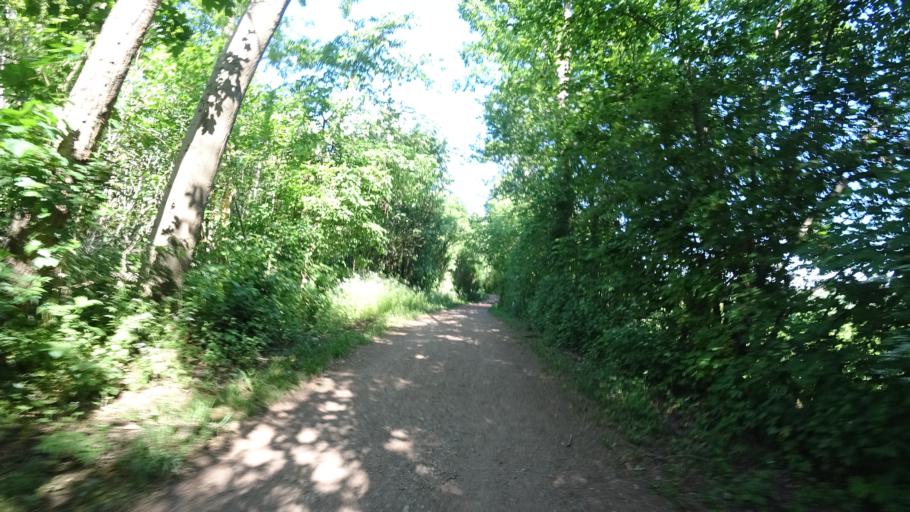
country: DE
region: North Rhine-Westphalia
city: Erwitte
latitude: 51.6367
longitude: 8.3648
